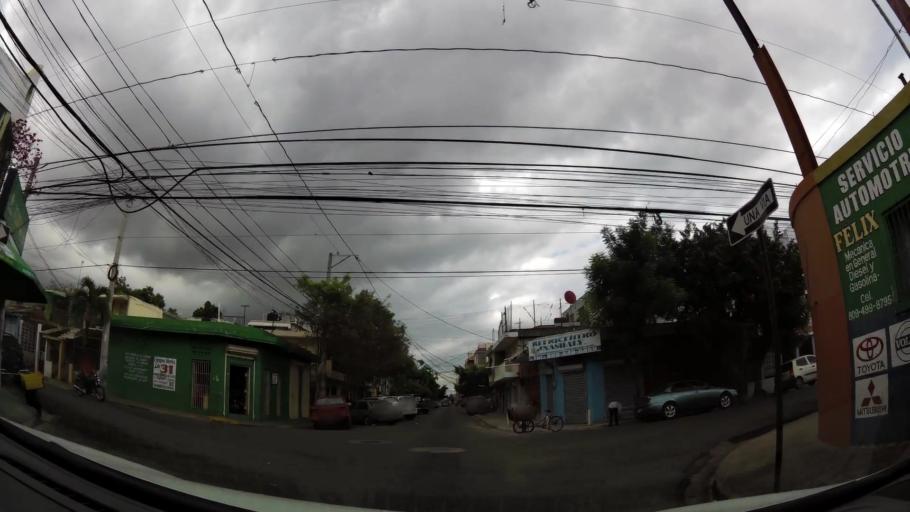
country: DO
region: Nacional
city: San Carlos
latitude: 18.4870
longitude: -69.9179
